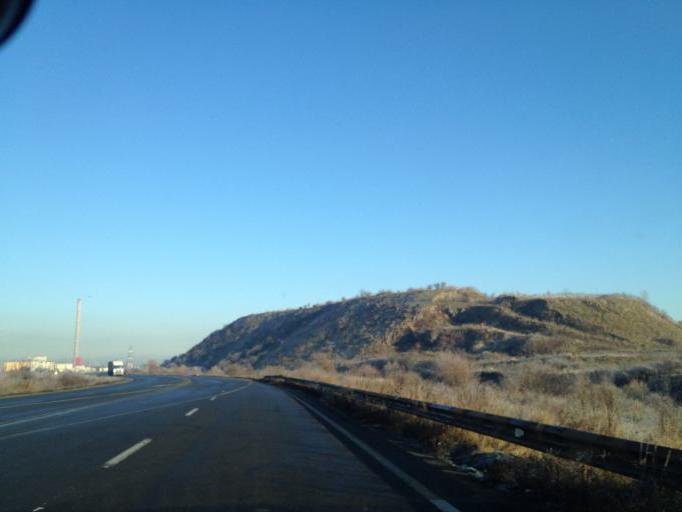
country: RO
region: Brasov
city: Brasov
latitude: 45.6390
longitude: 25.6568
